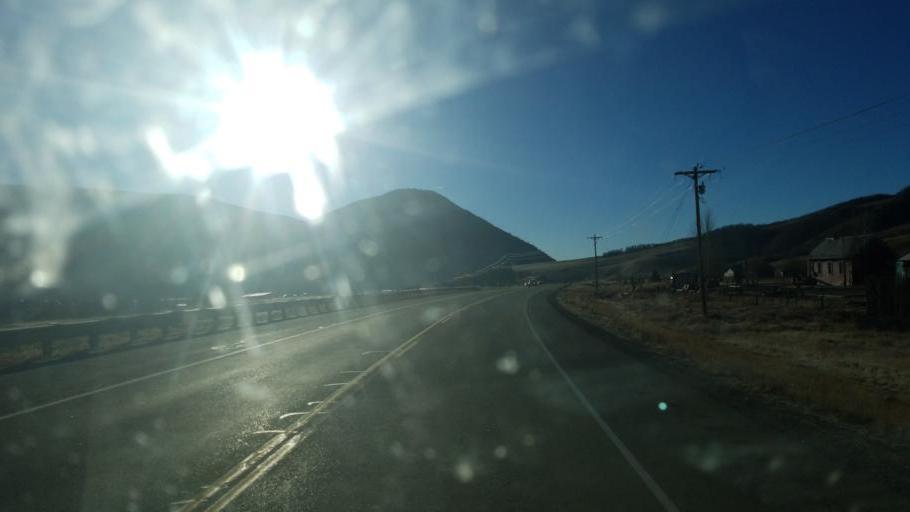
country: US
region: Colorado
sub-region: Gunnison County
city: Crested Butte
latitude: 38.8110
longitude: -106.8995
